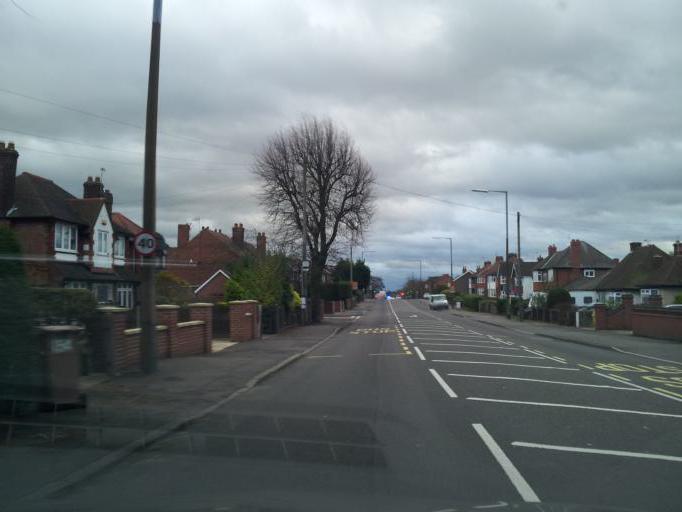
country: GB
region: England
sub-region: Derbyshire
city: Ilkeston
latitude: 52.9847
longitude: -1.3161
